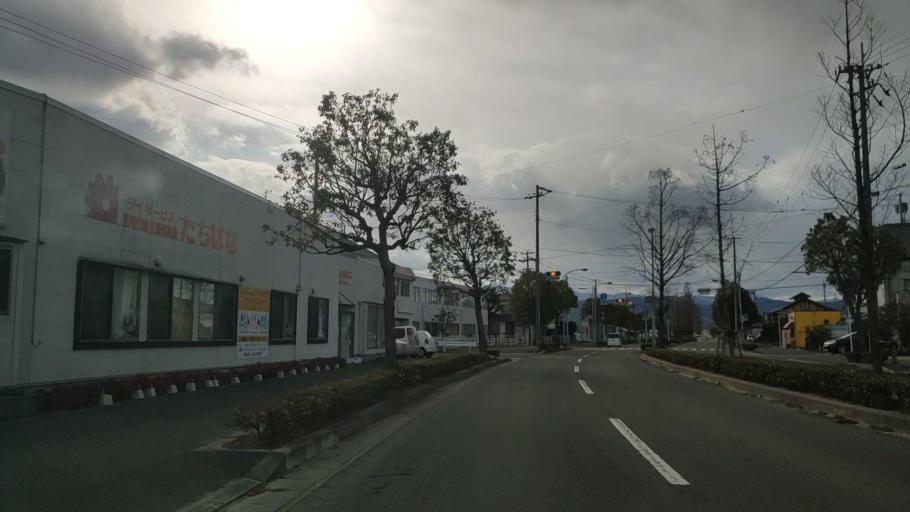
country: JP
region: Ehime
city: Saijo
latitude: 34.0503
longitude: 133.0112
